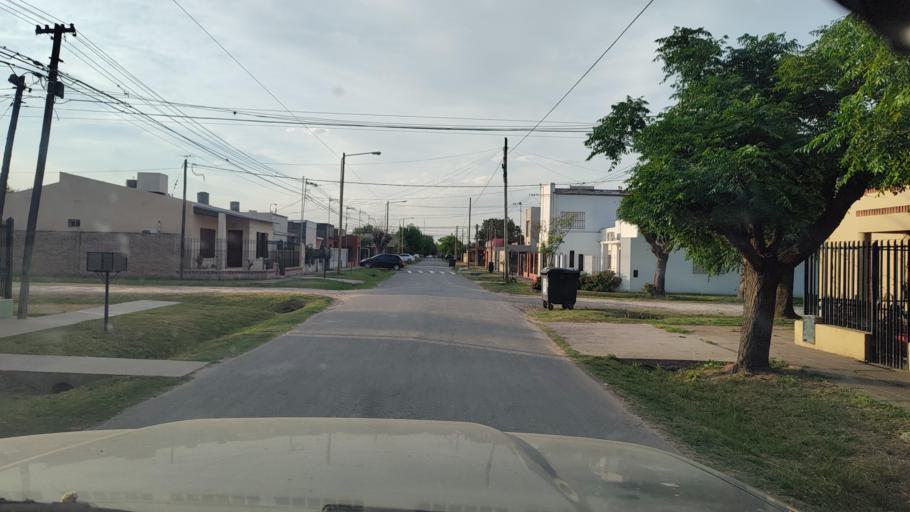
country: AR
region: Buenos Aires
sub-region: Partido de Lujan
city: Lujan
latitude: -34.5702
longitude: -59.1347
